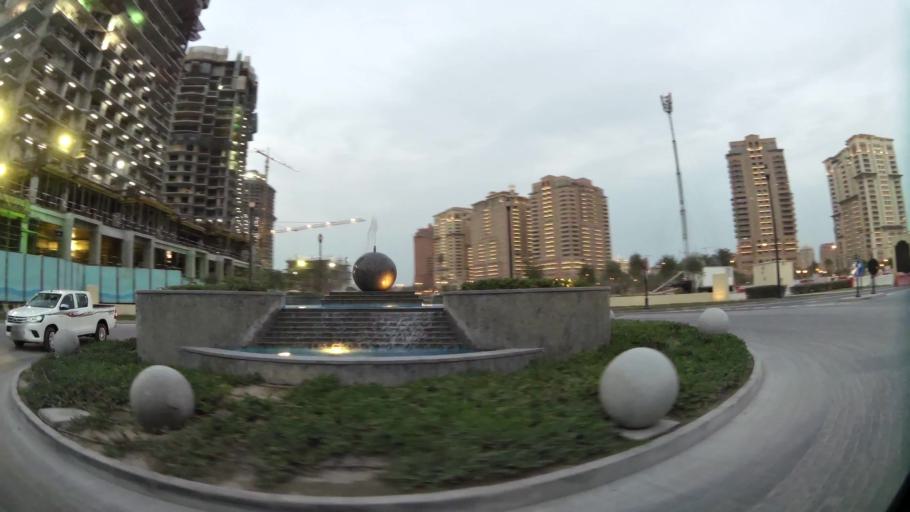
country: QA
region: Baladiyat ad Dawhah
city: Doha
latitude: 25.3727
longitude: 51.5366
